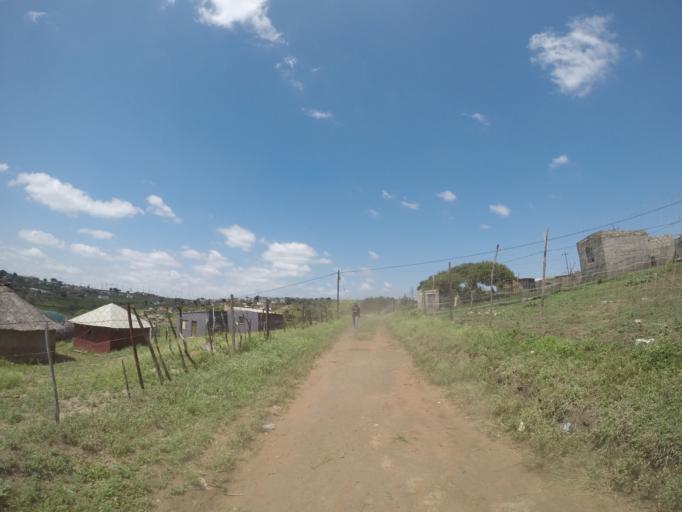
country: ZA
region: KwaZulu-Natal
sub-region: uThungulu District Municipality
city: Empangeni
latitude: -28.6036
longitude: 31.7362
